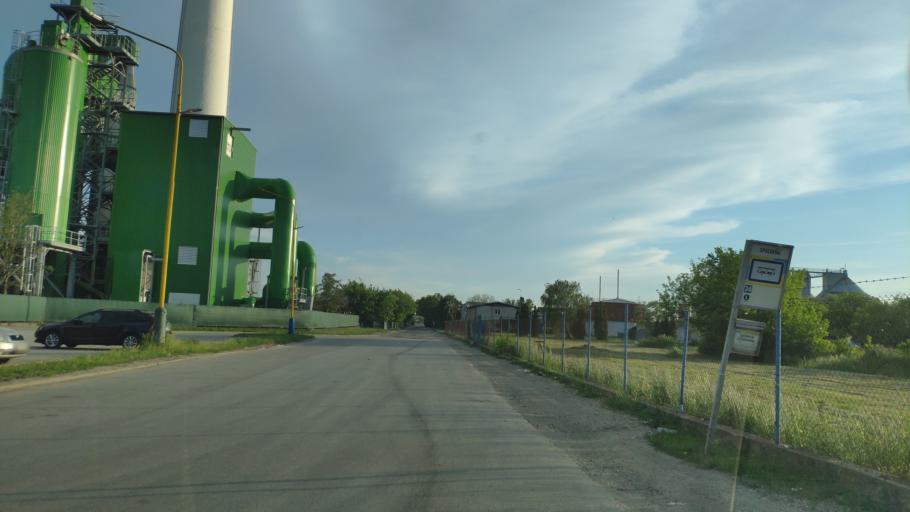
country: SK
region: Kosicky
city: Kosice
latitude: 48.6584
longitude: 21.3128
